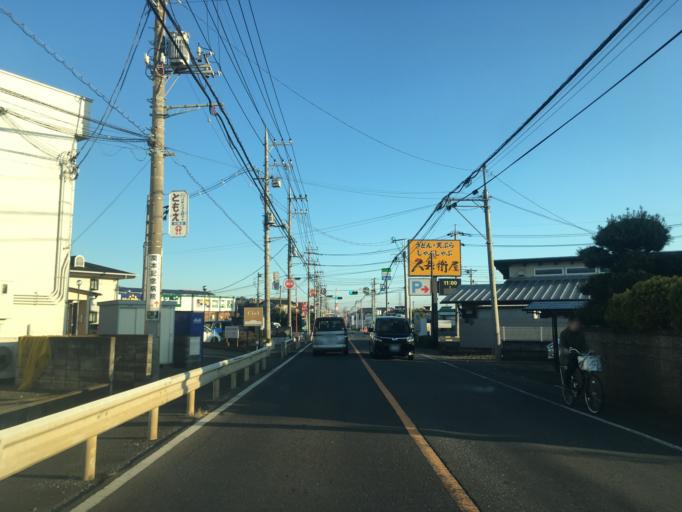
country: JP
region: Saitama
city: Kawagoe
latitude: 35.8833
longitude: 139.4761
